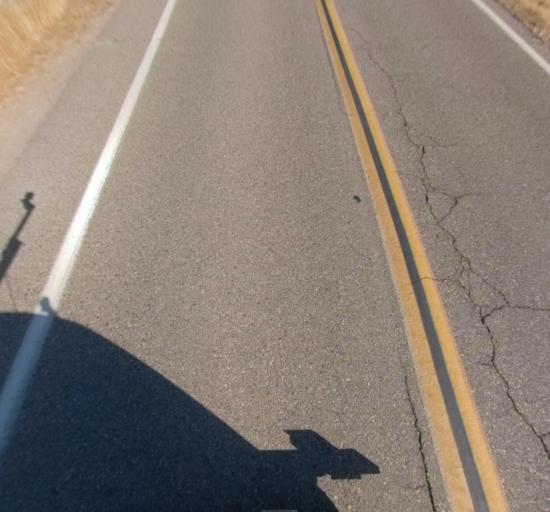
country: US
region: California
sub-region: Madera County
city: Madera Acres
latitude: 37.0007
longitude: -120.1071
